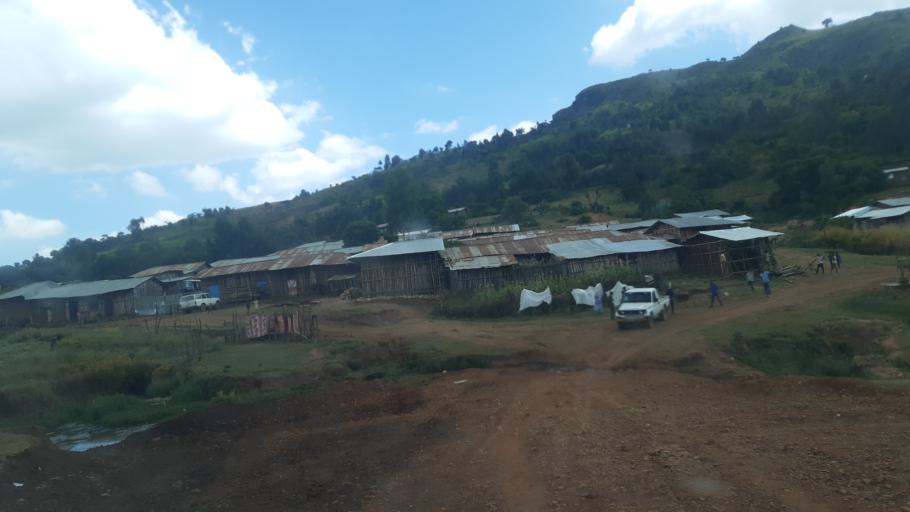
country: ET
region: Amhara
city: Dabat
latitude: 13.3382
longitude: 37.4219
